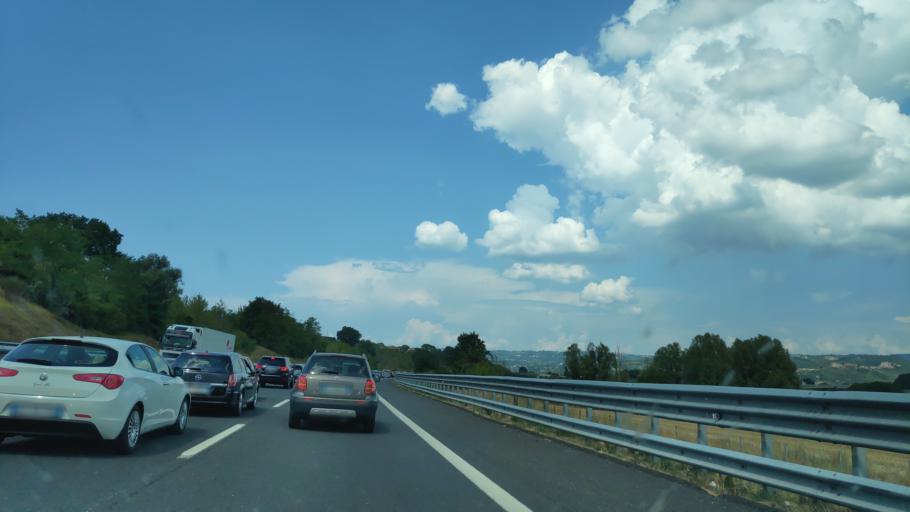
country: IT
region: Umbria
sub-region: Provincia di Terni
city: Fabro Scalo
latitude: 42.8498
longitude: 12.0379
